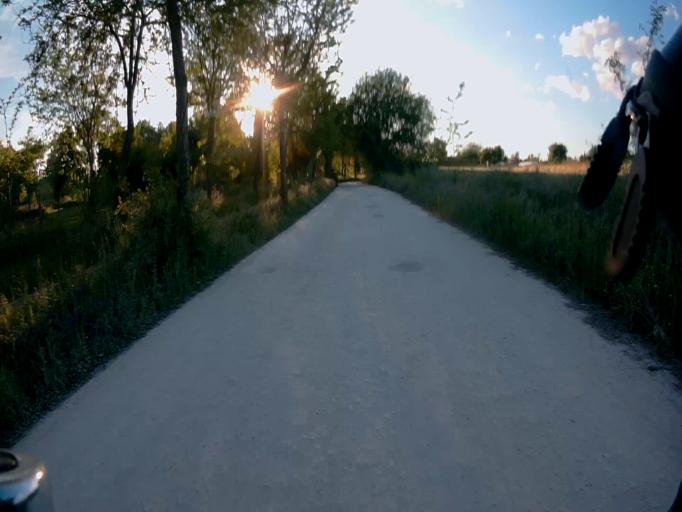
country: ES
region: Madrid
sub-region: Provincia de Madrid
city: Leganes
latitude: 40.3268
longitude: -3.7935
